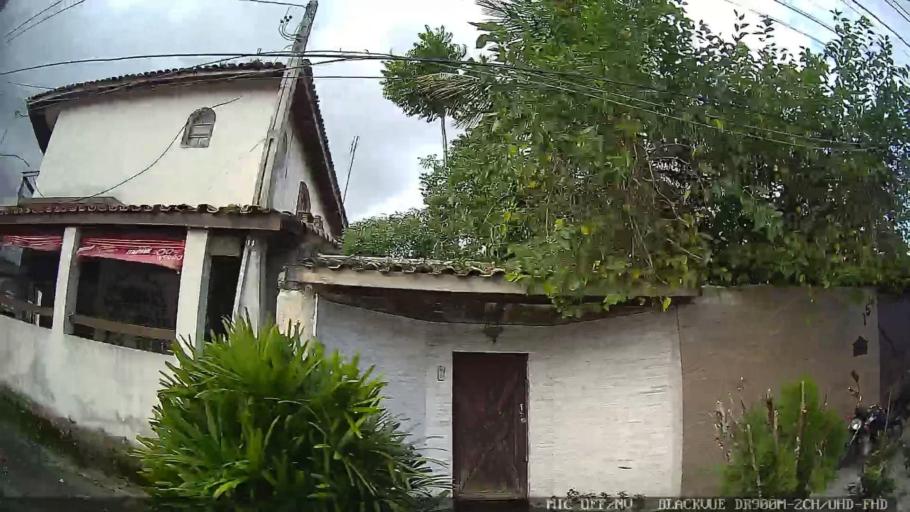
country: BR
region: Sao Paulo
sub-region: Caraguatatuba
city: Caraguatatuba
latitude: -23.6277
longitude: -45.4288
